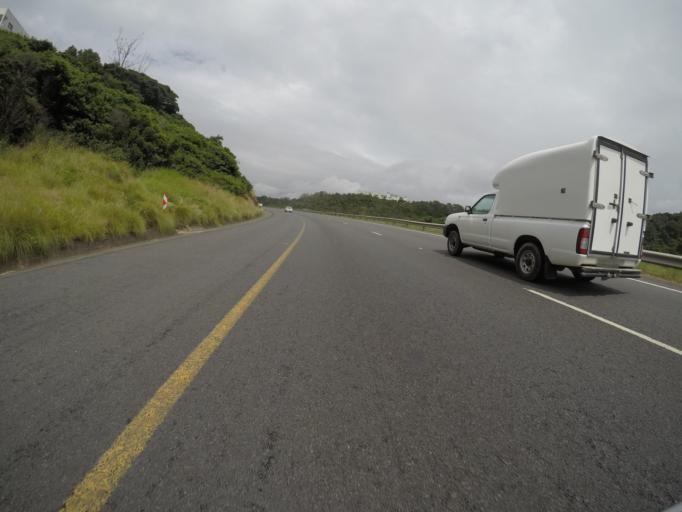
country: ZA
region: Eastern Cape
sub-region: Buffalo City Metropolitan Municipality
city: East London
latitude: -32.9707
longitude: 27.9076
